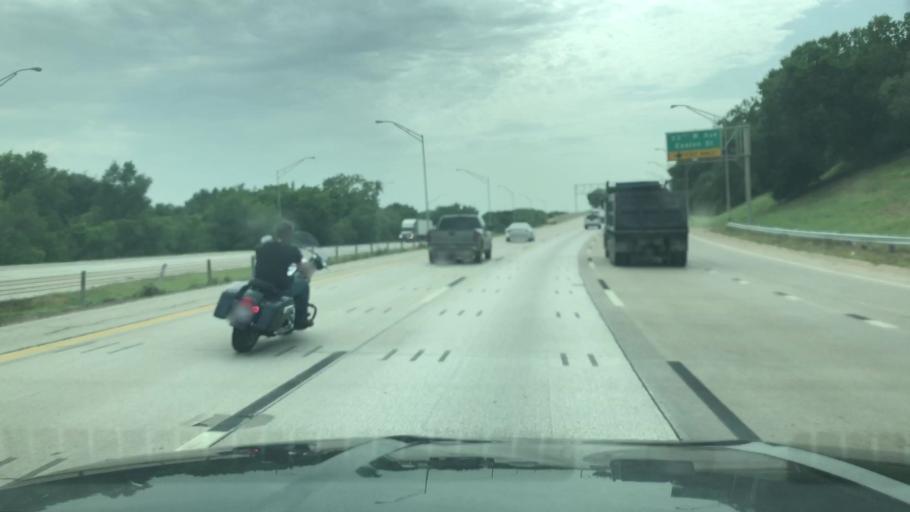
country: US
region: Oklahoma
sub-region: Tulsa County
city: Tulsa
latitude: 36.1565
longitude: -96.0246
